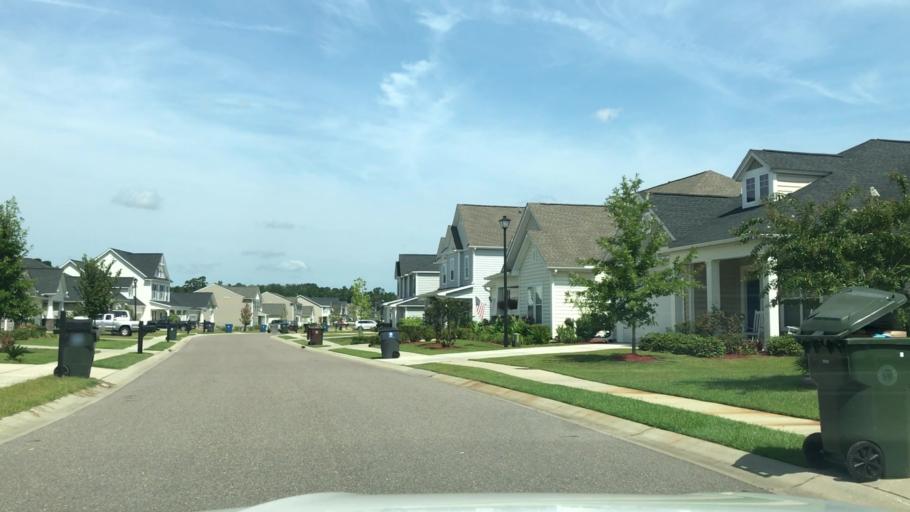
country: US
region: South Carolina
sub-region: Berkeley County
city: Moncks Corner
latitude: 33.1058
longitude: -80.0428
